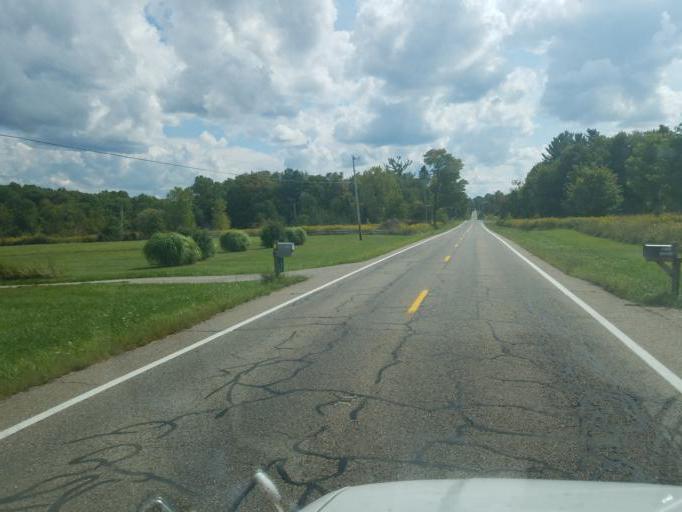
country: US
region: Ohio
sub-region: Portage County
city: Hiram
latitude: 41.3473
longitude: -81.1432
